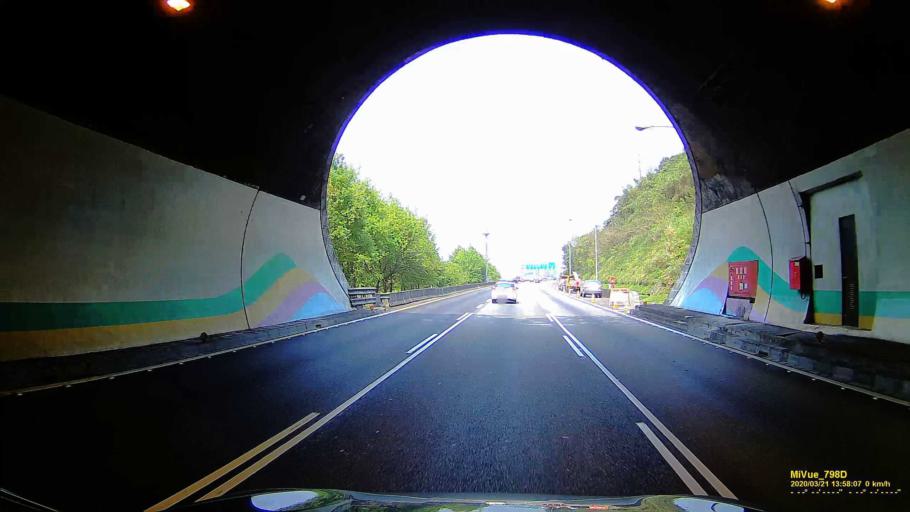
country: TW
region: Taipei
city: Taipei
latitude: 24.9689
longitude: 121.5498
